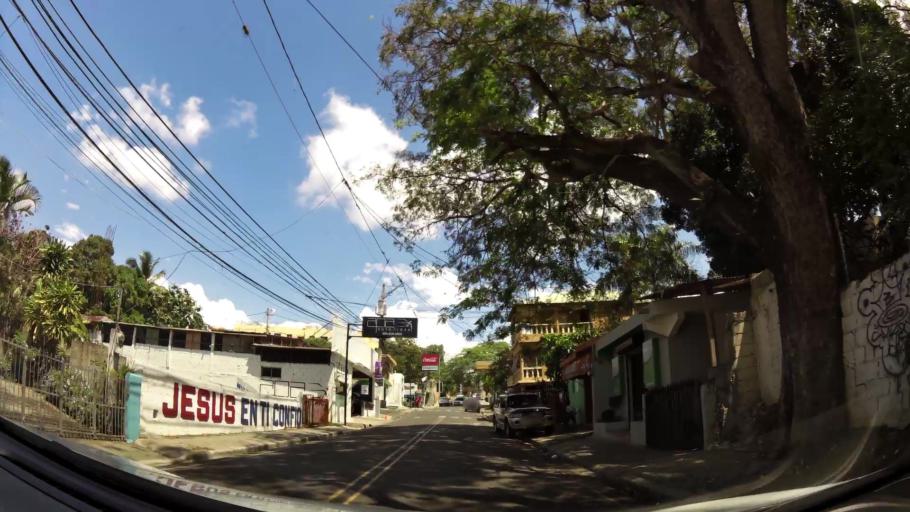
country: DO
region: Santiago
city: Santiago de los Caballeros
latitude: 19.4633
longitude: -70.6766
